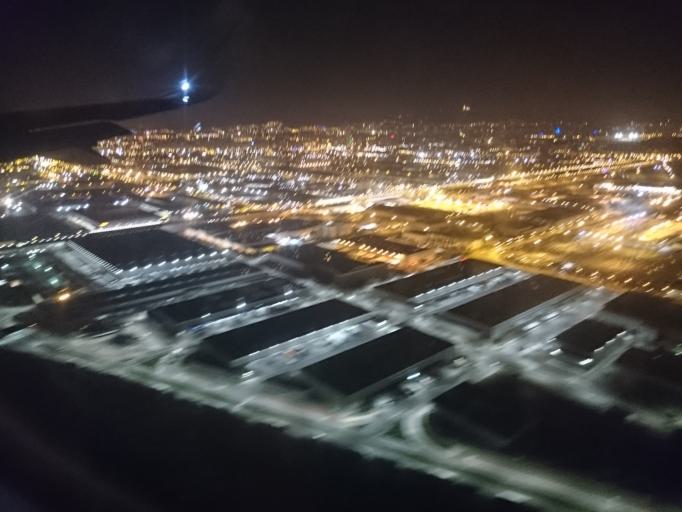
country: ES
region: Catalonia
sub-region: Provincia de Barcelona
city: El Prat de Llobregat
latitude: 41.3193
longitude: 2.1436
